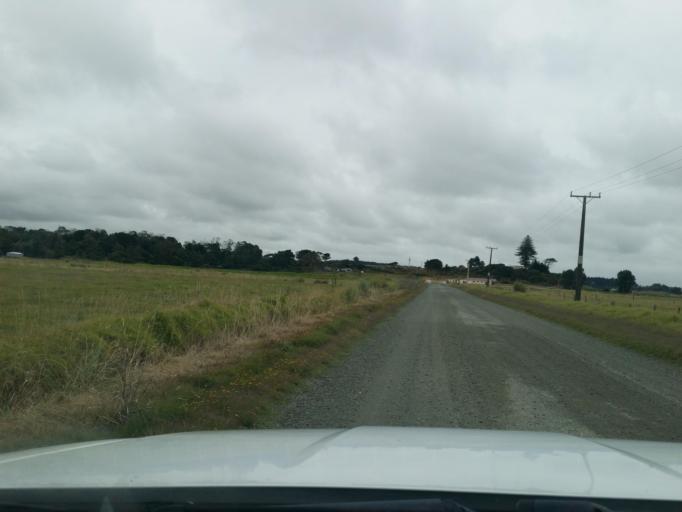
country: NZ
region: Northland
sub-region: Kaipara District
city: Dargaville
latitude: -36.0106
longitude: 173.8898
